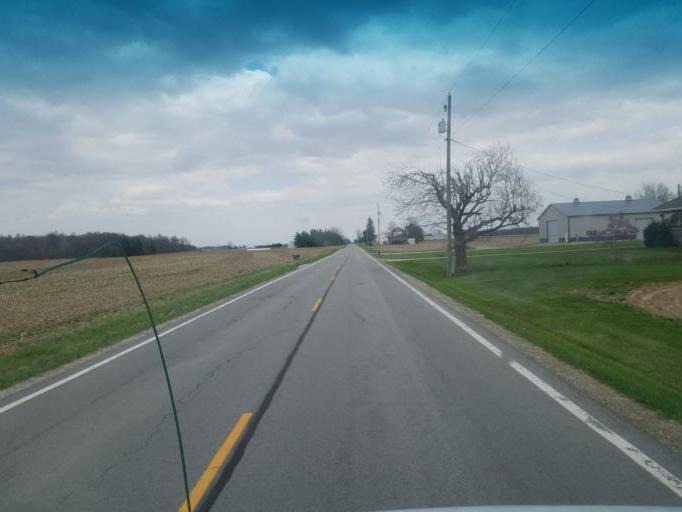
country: US
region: Ohio
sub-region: Crawford County
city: Bucyrus
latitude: 40.9504
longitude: -83.0536
